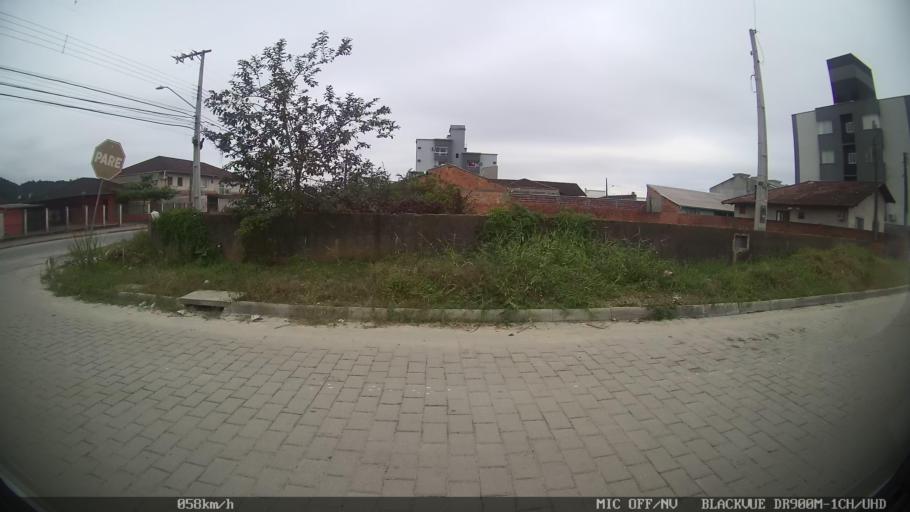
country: BR
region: Santa Catarina
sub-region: Joinville
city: Joinville
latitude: -26.2985
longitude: -48.9001
